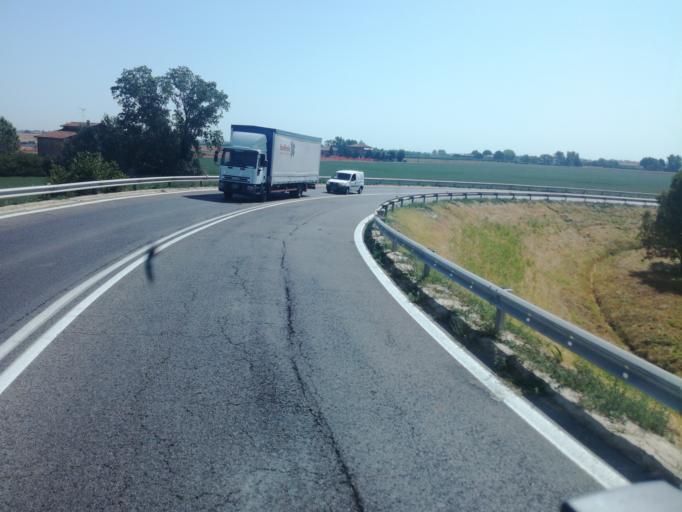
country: IT
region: Emilia-Romagna
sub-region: Provincia di Bologna
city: Castel San Pietro Terme
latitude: 44.4268
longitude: 11.6091
